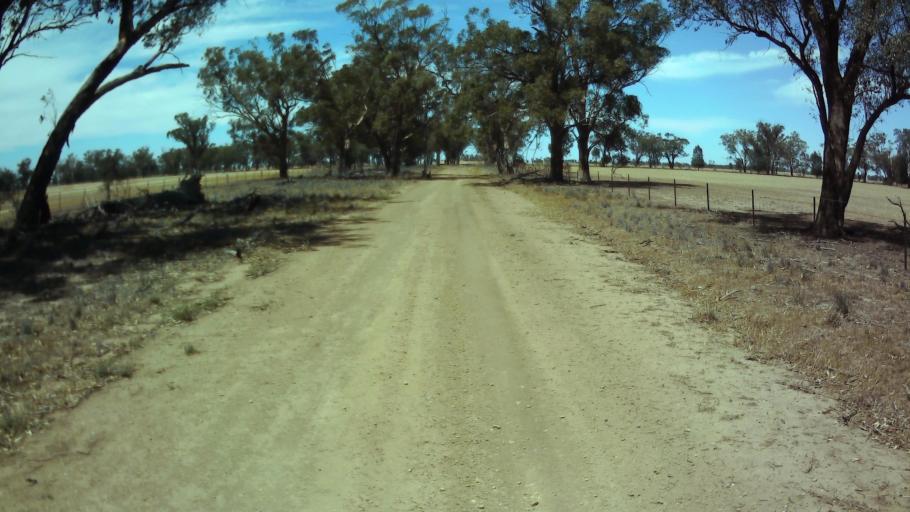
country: AU
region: New South Wales
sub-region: Weddin
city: Grenfell
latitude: -33.9301
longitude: 147.8029
